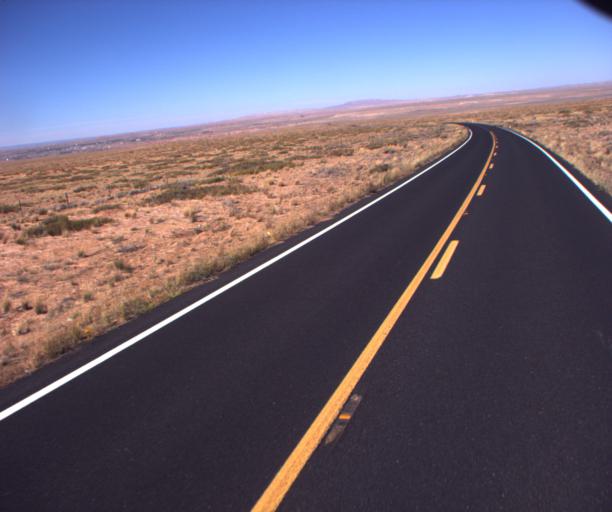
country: US
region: Arizona
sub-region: Coconino County
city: Tuba City
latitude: 36.0493
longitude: -111.1812
